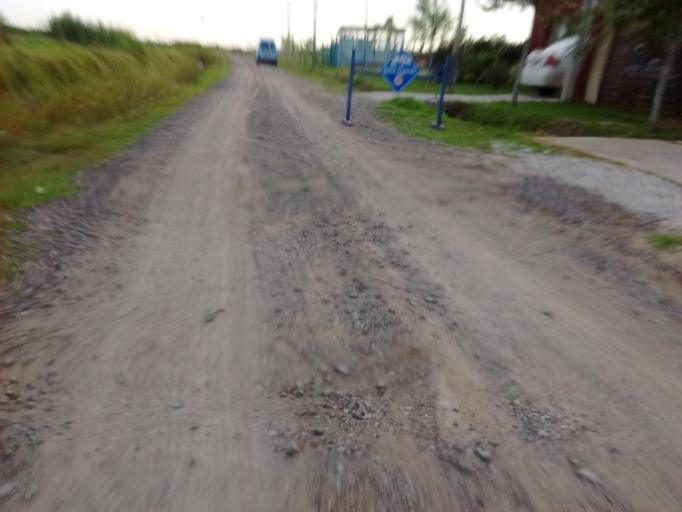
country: AR
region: Santa Fe
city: Roldan
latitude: -32.9398
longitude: -60.8747
